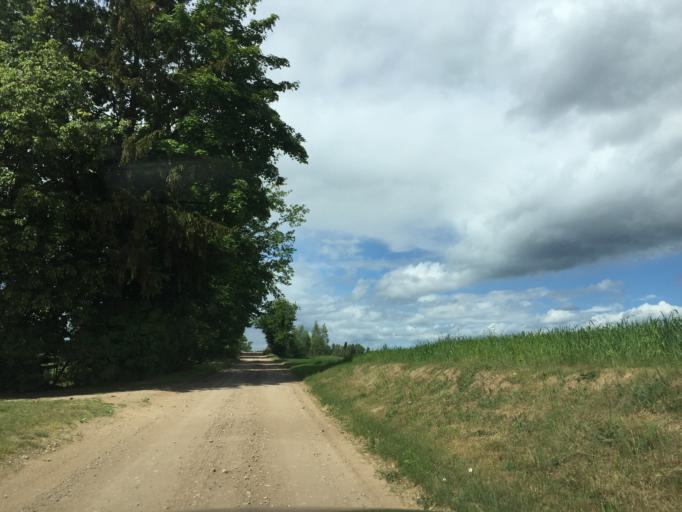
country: LV
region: Lecava
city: Iecava
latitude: 56.5629
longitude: 24.1336
